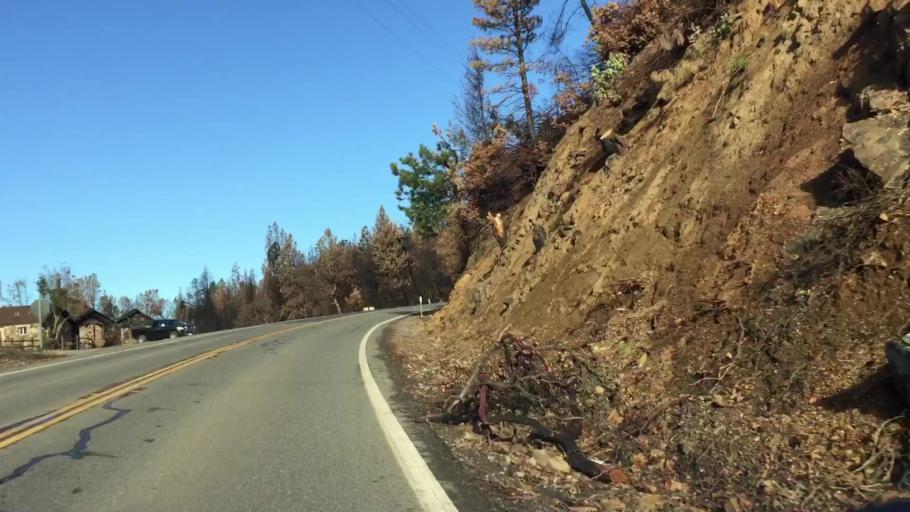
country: US
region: California
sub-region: Butte County
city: Magalia
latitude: 39.7340
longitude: -121.4961
